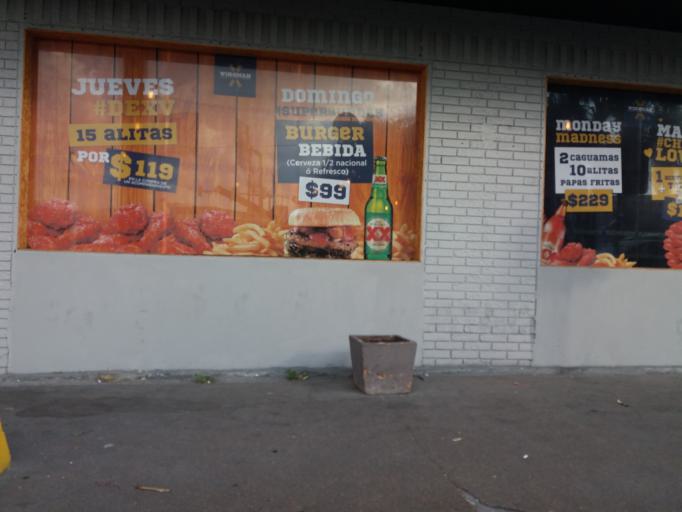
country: MX
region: Nuevo Leon
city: Garza Garcia
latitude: 25.7118
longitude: -100.3774
